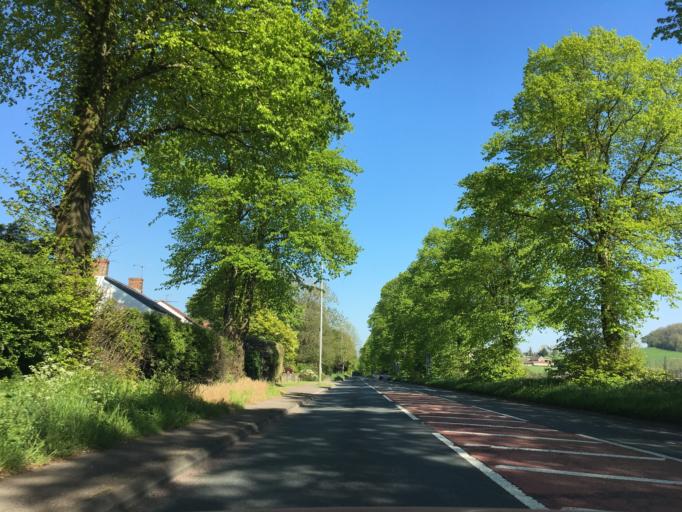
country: GB
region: Wales
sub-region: Newport
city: Llanvaches
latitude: 51.6159
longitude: -2.8433
